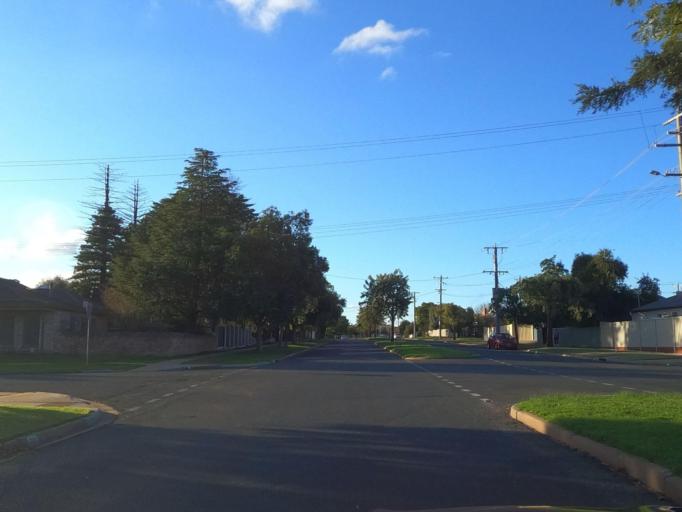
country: AU
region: Victoria
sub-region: Swan Hill
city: Swan Hill
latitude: -35.3467
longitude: 143.5556
